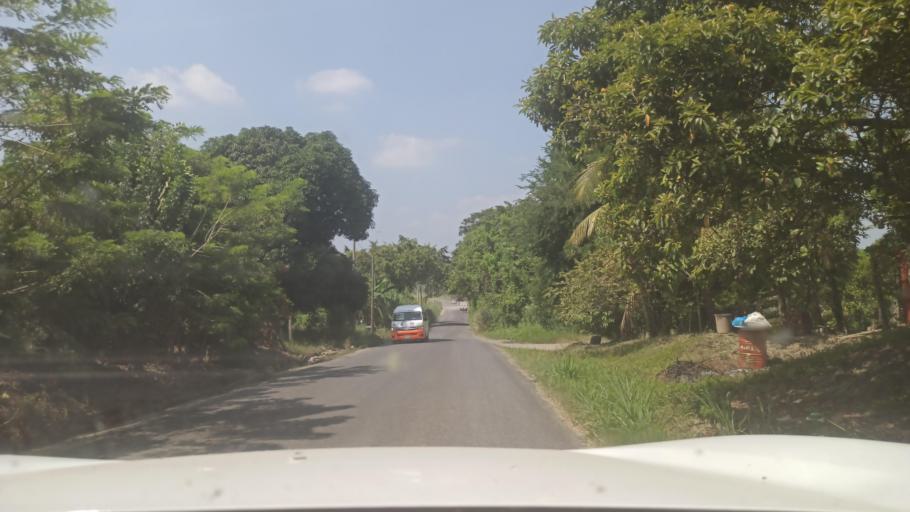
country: MX
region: Veracruz
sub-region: Atzalan
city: Colonias Pedernales
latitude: 20.0474
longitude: -97.0072
